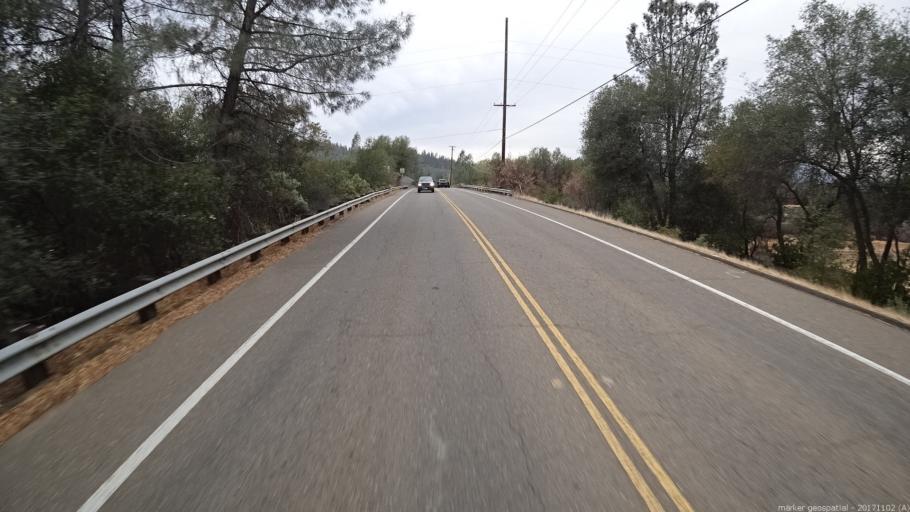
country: US
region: California
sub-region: Shasta County
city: Central Valley (historical)
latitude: 40.6634
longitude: -122.3929
